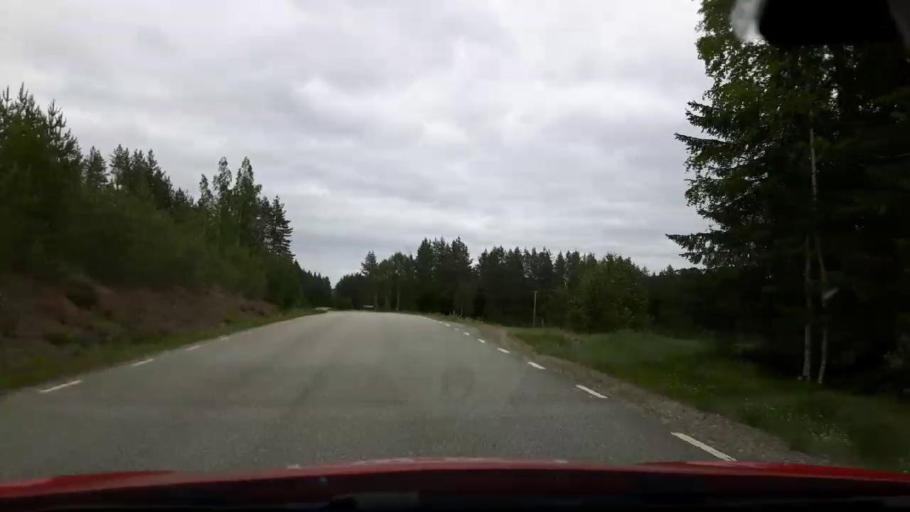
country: SE
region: Jaemtland
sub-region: Ragunda Kommun
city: Hammarstrand
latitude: 63.2097
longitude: 16.0101
